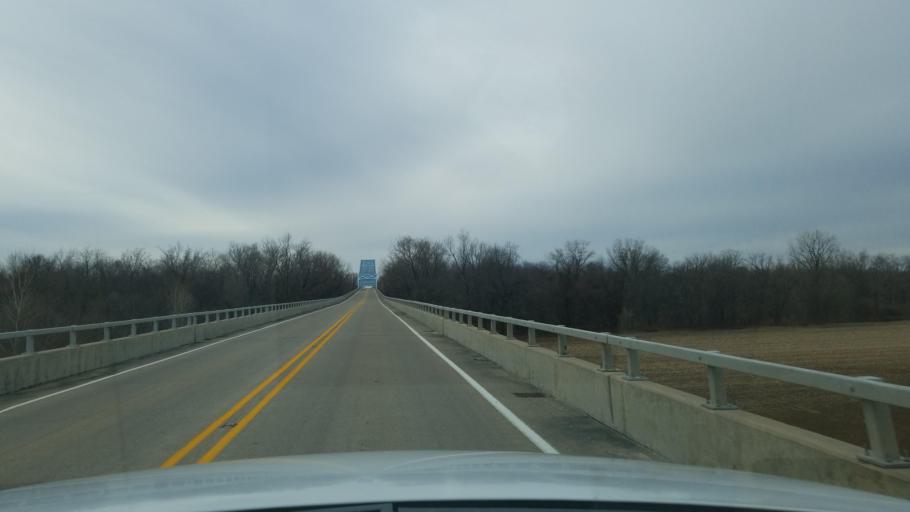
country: US
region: Indiana
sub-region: Posey County
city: Mount Vernon
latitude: 37.9441
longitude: -88.0296
